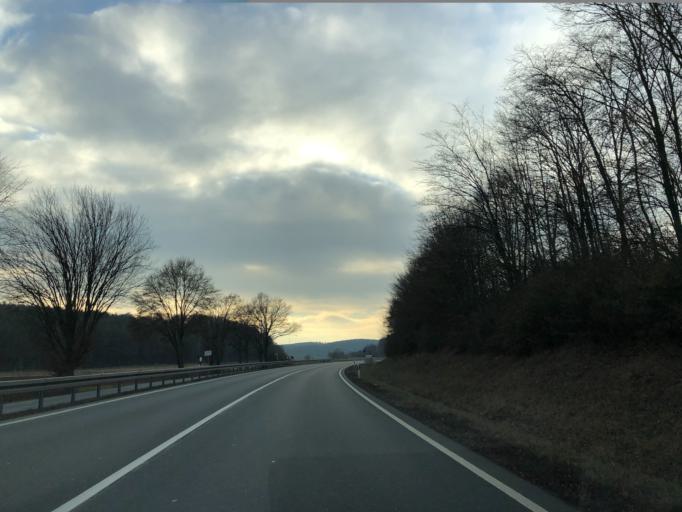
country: DE
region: Bavaria
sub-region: Regierungsbezirk Unterfranken
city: Hettstadt
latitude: 49.7800
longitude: 9.8082
